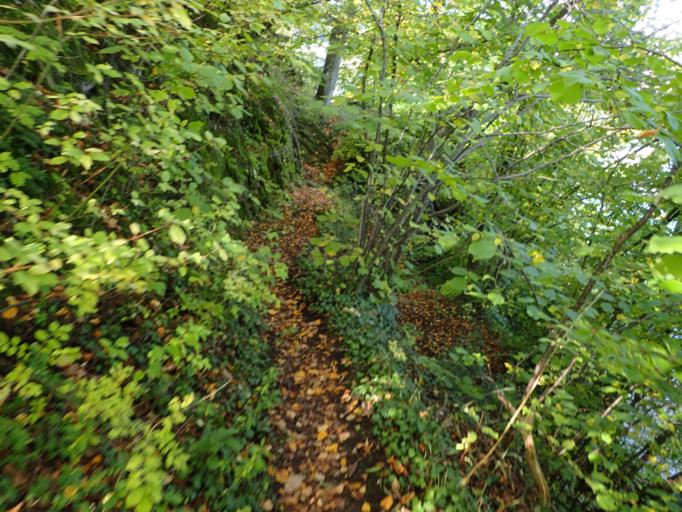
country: AT
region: Salzburg
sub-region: Politischer Bezirk Salzburg-Umgebung
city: Mattsee
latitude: 47.9710
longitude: 13.1077
